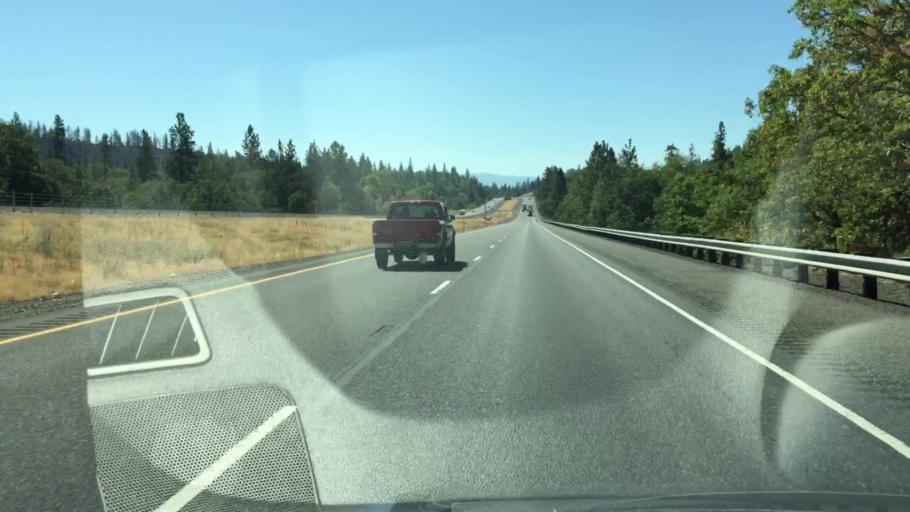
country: US
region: Oregon
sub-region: Josephine County
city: Merlin
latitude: 42.5403
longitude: -123.3704
